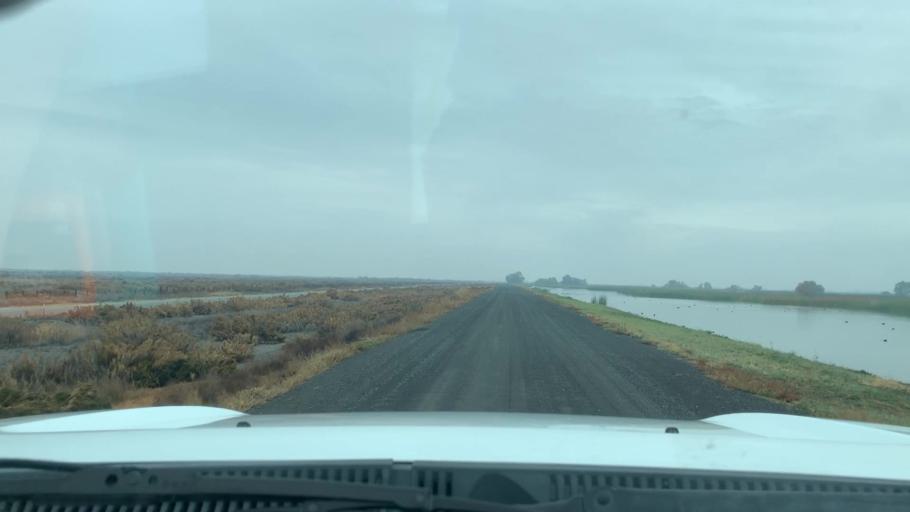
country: US
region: California
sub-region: Kern County
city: Lost Hills
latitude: 35.7418
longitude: -119.5799
